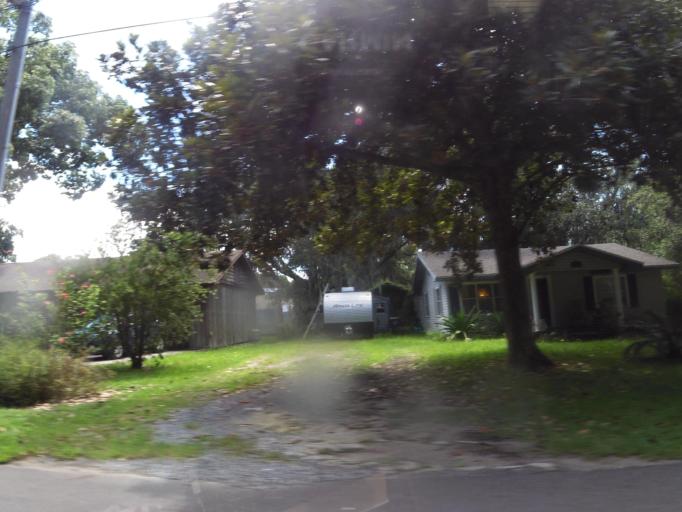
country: US
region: Florida
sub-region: Nassau County
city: Fernandina Beach
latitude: 30.6344
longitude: -81.4618
